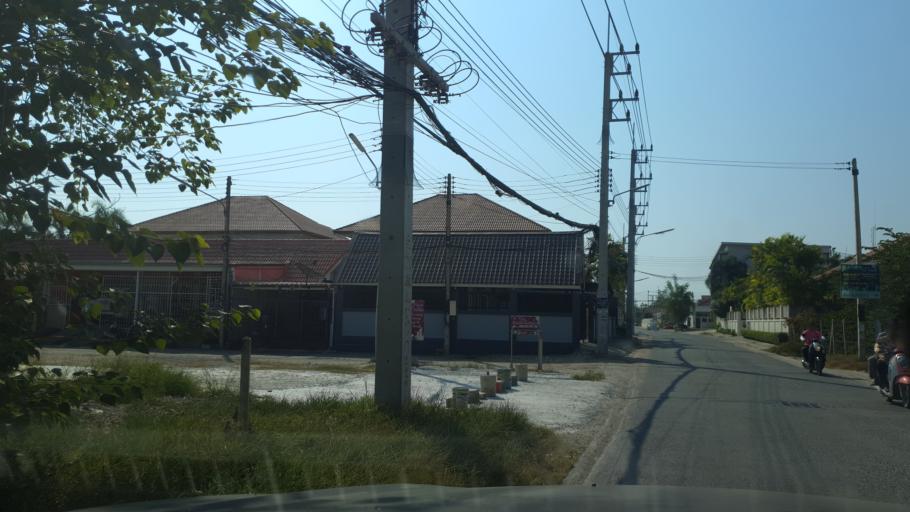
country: TH
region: Prachuap Khiri Khan
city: Hua Hin
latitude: 12.5523
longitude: 99.9540
